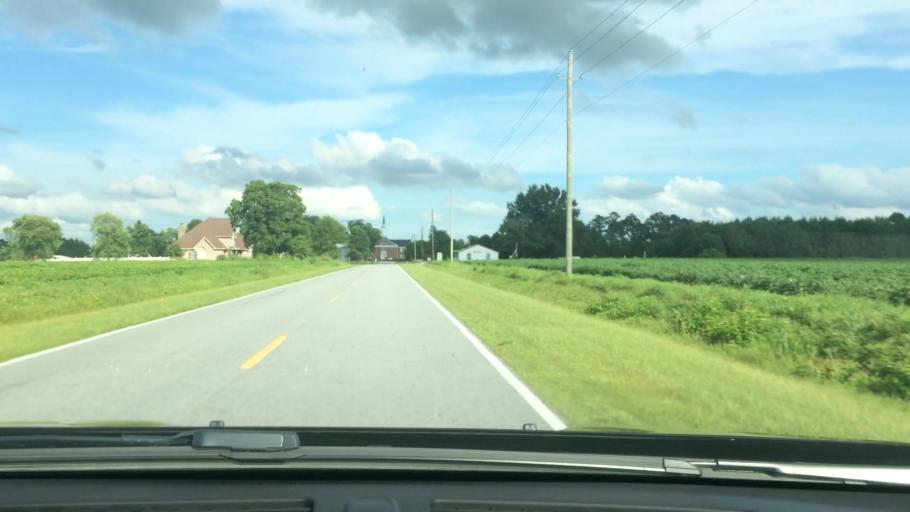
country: US
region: North Carolina
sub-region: Pitt County
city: Ayden
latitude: 35.4320
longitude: -77.4146
